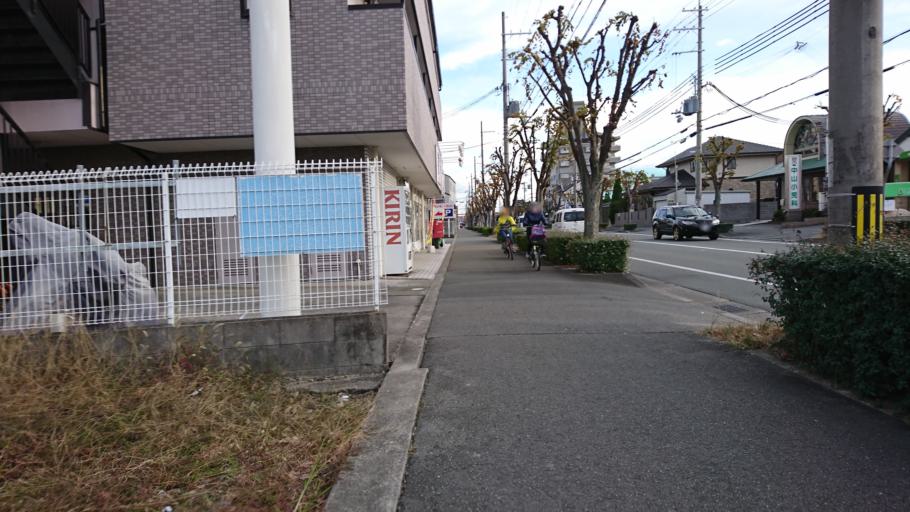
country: JP
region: Hyogo
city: Kakogawacho-honmachi
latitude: 34.7522
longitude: 134.8401
